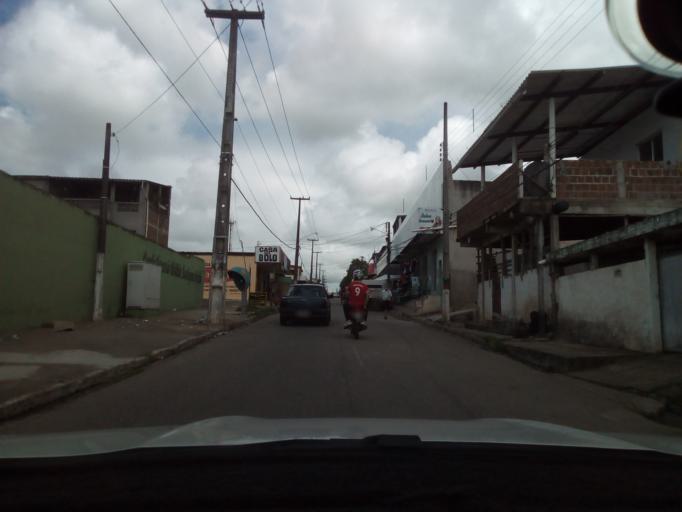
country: BR
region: Paraiba
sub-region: Bayeux
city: Bayeux
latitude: -7.1438
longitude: -34.9235
